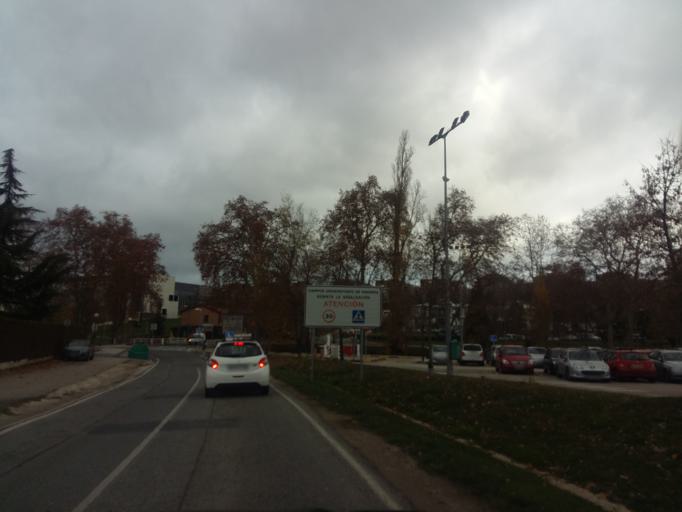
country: ES
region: Navarre
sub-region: Provincia de Navarra
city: Iturrama
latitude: 42.7984
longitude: -1.6532
